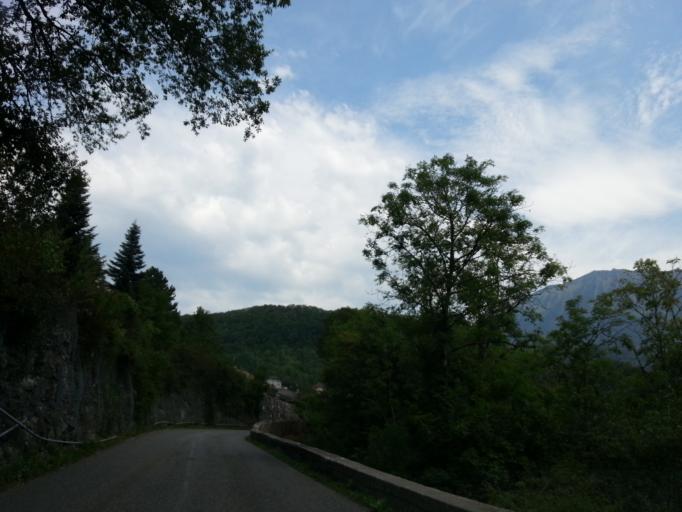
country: FR
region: Rhone-Alpes
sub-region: Departement de la Haute-Savoie
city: Faverges
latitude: 45.7415
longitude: 6.2944
